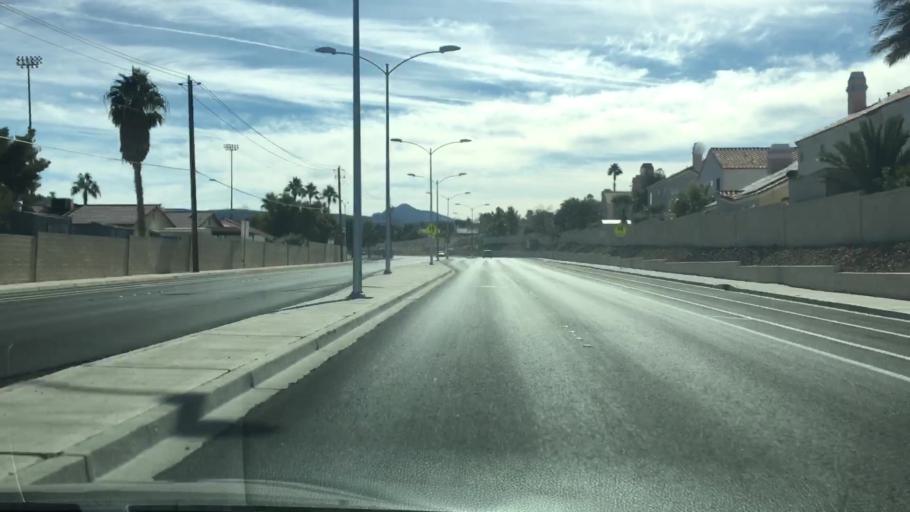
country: US
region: Nevada
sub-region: Clark County
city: Whitney
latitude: 36.0611
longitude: -115.0587
